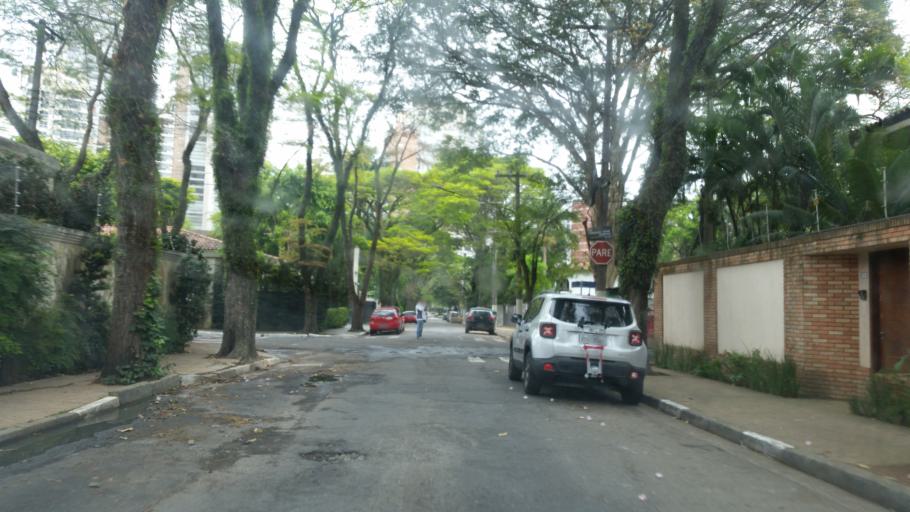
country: BR
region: Sao Paulo
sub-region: Sao Paulo
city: Sao Paulo
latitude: -23.5952
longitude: -46.6614
